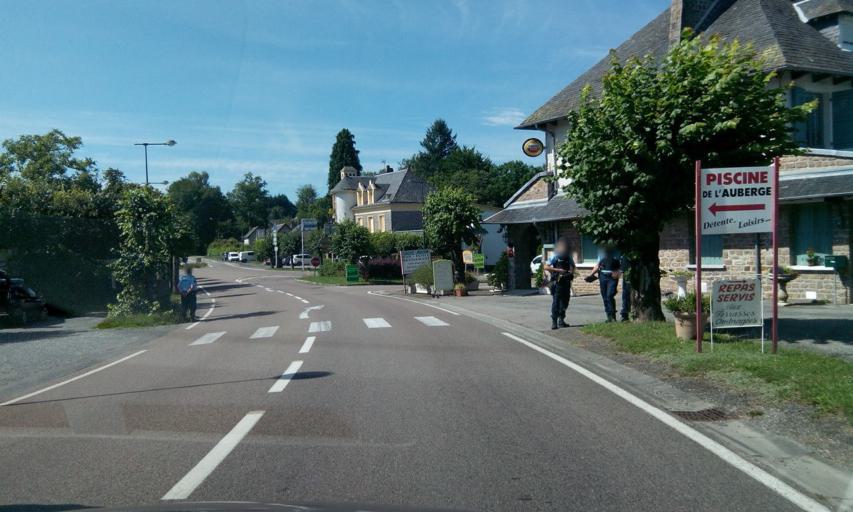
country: FR
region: Limousin
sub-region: Departement de la Correze
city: Beynat
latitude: 45.1352
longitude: 1.7831
